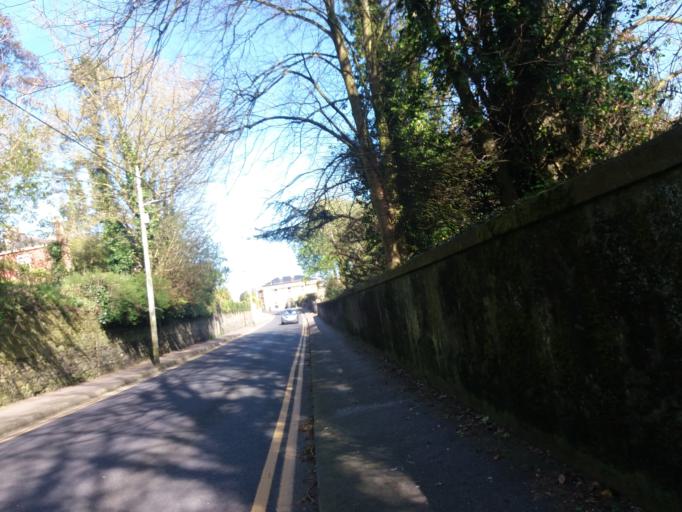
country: IE
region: Munster
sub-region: County Cork
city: Cork
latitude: 51.9046
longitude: -8.4567
